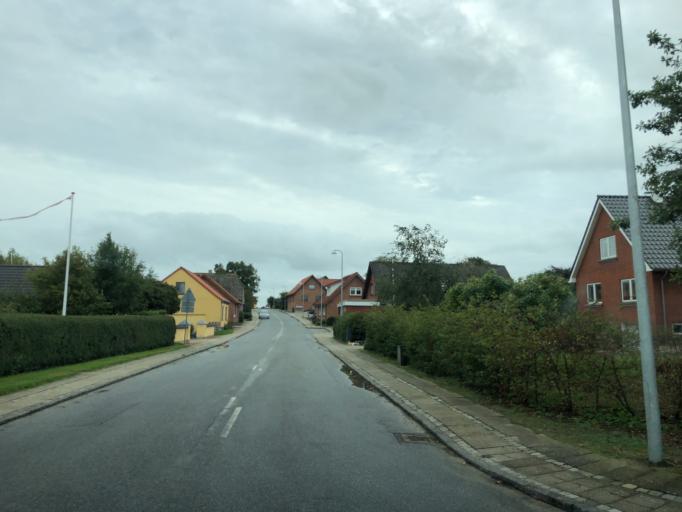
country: DK
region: Central Jutland
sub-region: Herning Kommune
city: Vildbjerg
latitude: 56.1791
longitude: 8.7438
